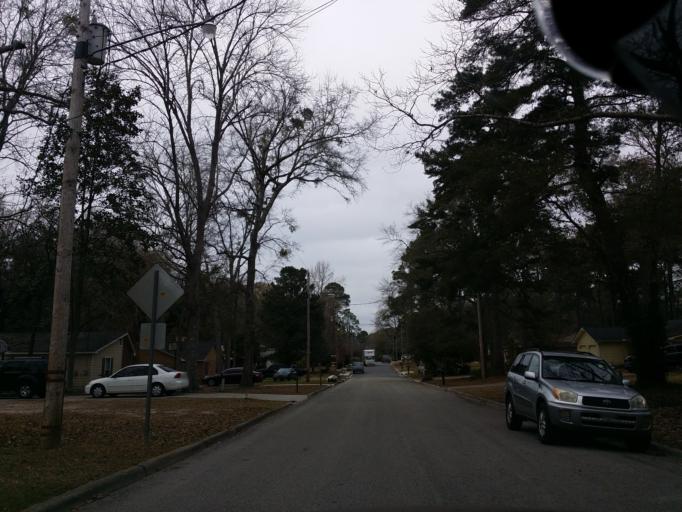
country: US
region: Florida
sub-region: Leon County
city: Tallahassee
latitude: 30.5022
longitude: -84.2266
